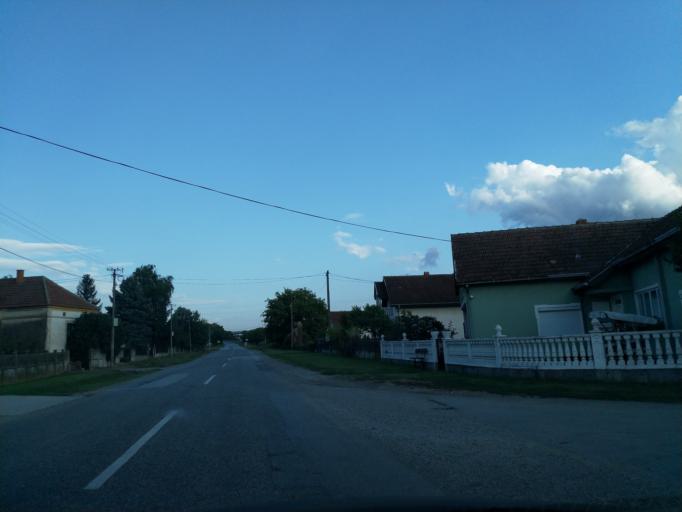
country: RS
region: Central Serbia
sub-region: Rasinski Okrug
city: Cicevac
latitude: 43.7528
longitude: 21.4389
